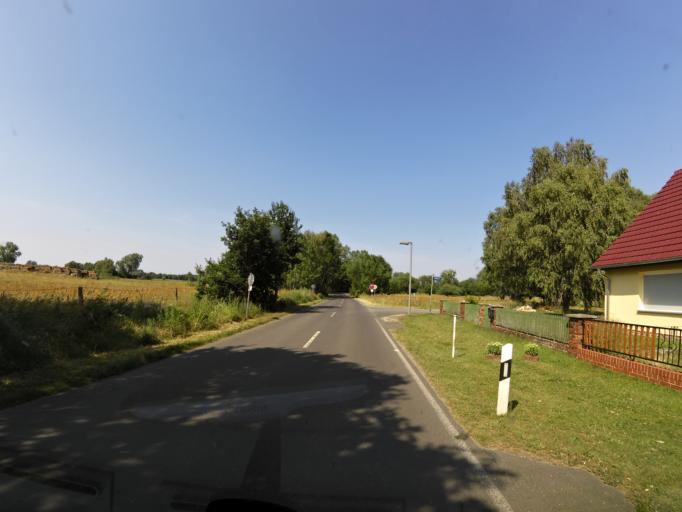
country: DE
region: Brandenburg
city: Zehdenick
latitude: 53.0238
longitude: 13.2919
